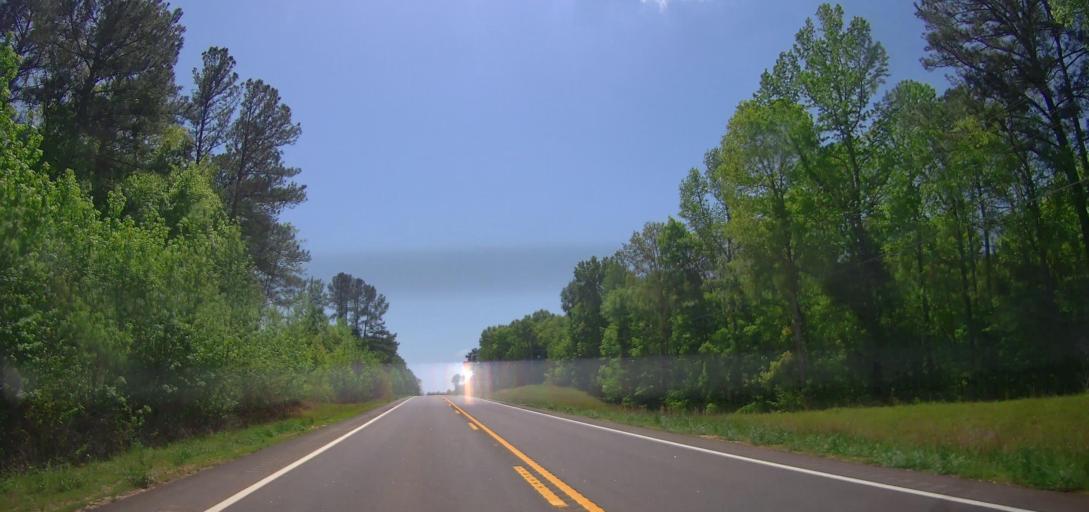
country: US
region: Georgia
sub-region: Putnam County
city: Eatonton
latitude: 33.2607
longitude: -83.4192
